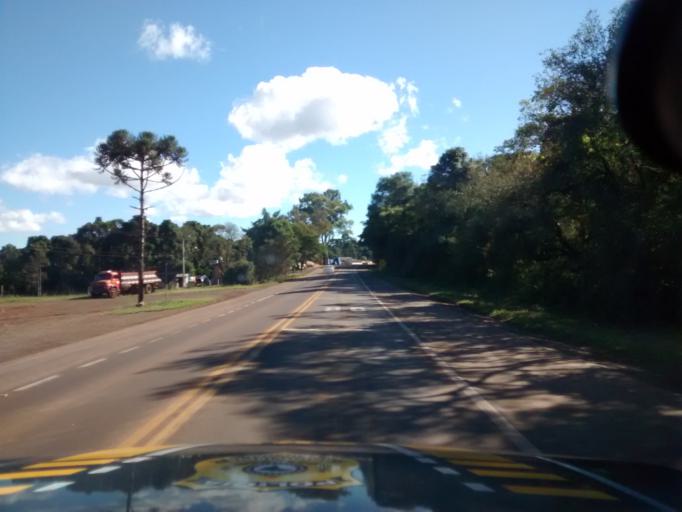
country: BR
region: Rio Grande do Sul
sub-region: Vacaria
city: Vacaria
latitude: -28.3247
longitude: -51.1972
